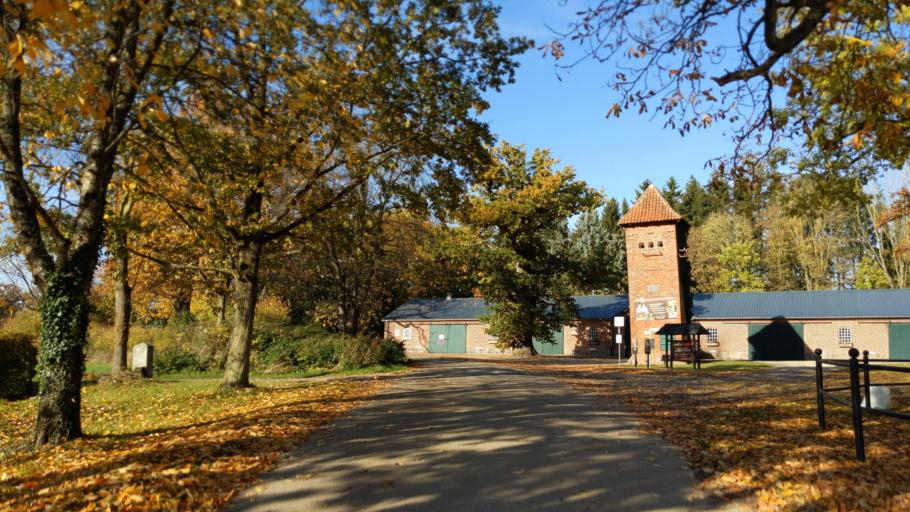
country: DE
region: Schleswig-Holstein
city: Neustadt in Holstein
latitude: 54.1293
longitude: 10.7721
